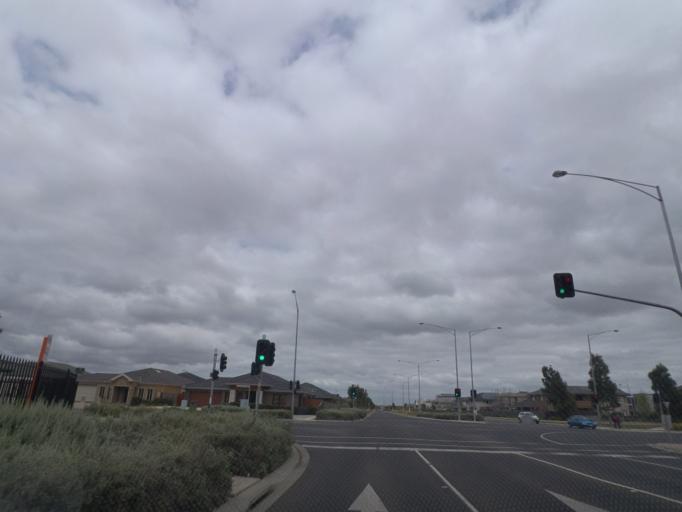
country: AU
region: Victoria
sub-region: Melton
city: Burnside Heights
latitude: -37.7301
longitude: 144.7497
